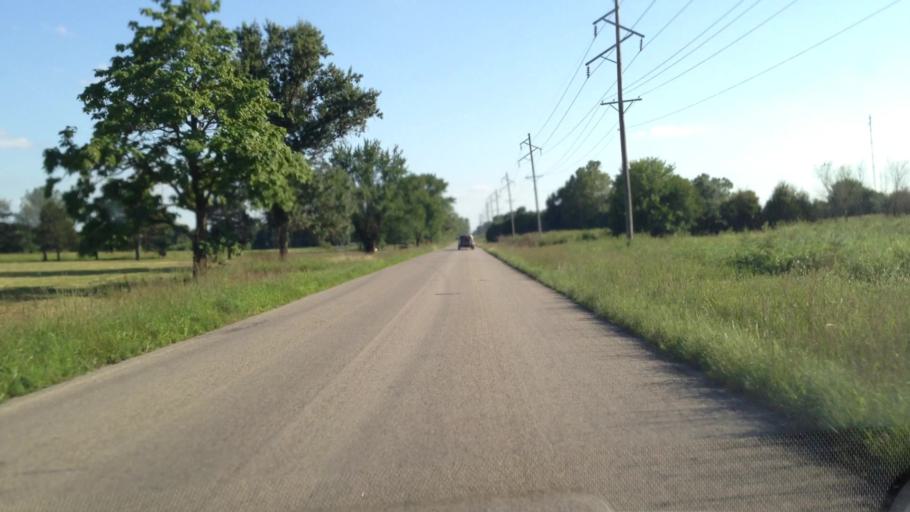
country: US
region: Kansas
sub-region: Crawford County
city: Frontenac
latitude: 37.4597
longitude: -94.6308
